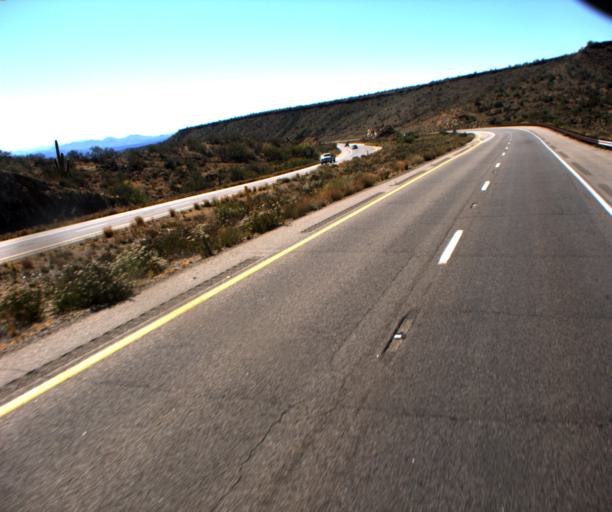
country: US
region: Arizona
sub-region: Yavapai County
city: Bagdad
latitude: 34.4537
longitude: -113.2889
